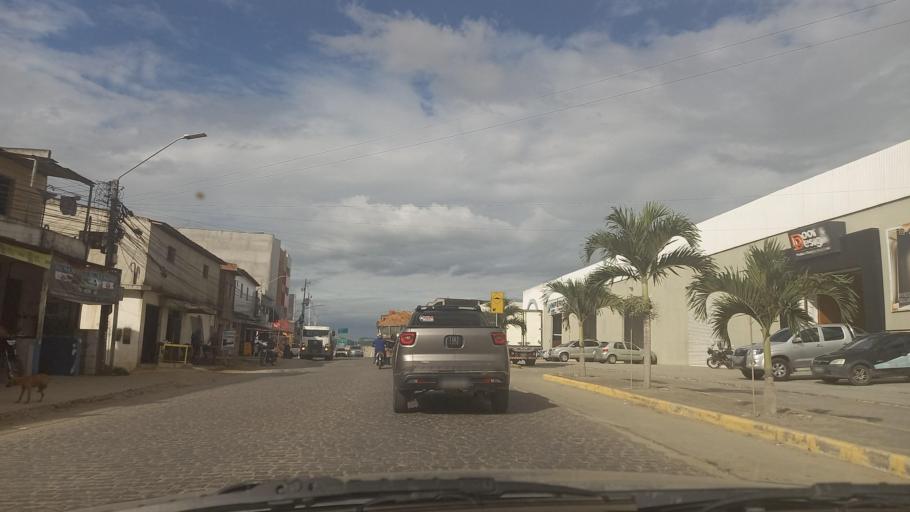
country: BR
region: Pernambuco
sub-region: Caruaru
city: Caruaru
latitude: -8.2878
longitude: -36.0059
